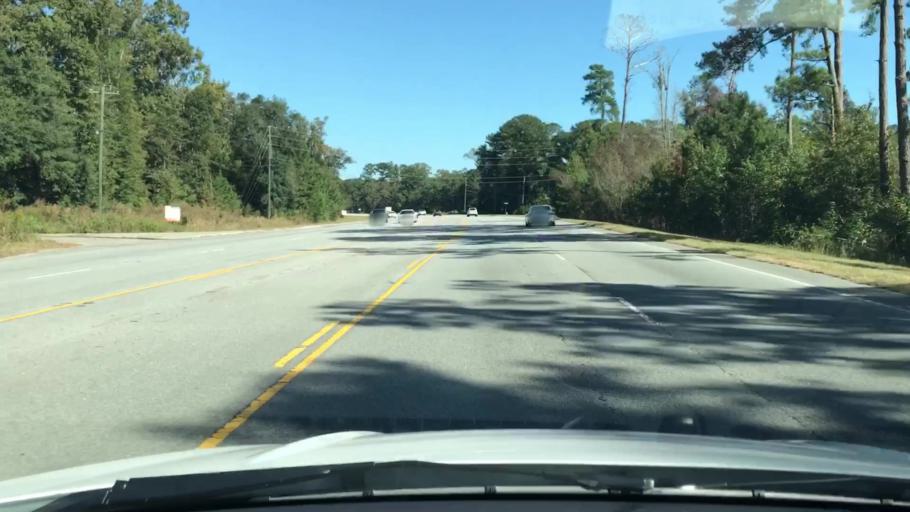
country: US
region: South Carolina
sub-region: Beaufort County
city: Bluffton
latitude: 32.3578
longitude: -80.8776
